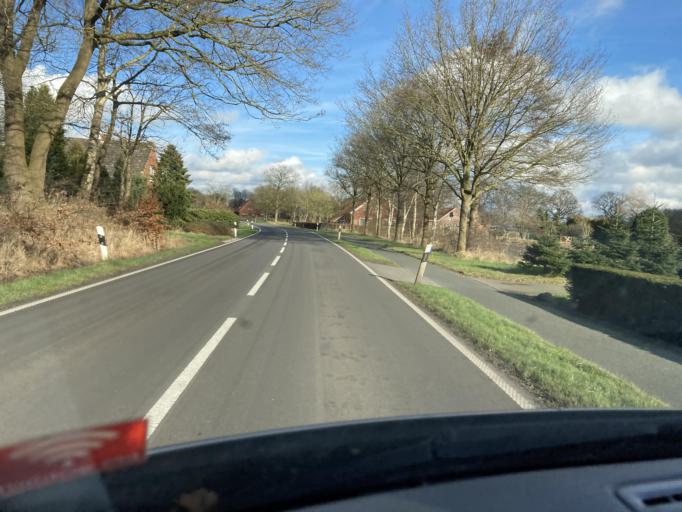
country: DE
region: Lower Saxony
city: Schwerinsdorf
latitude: 53.2683
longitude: 7.7095
